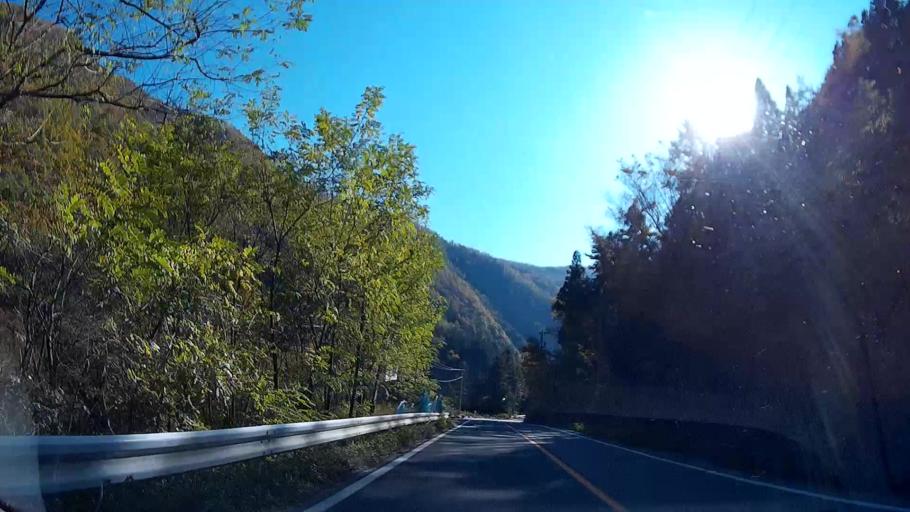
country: JP
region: Nagano
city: Toyoshina
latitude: 36.1764
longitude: 137.7810
